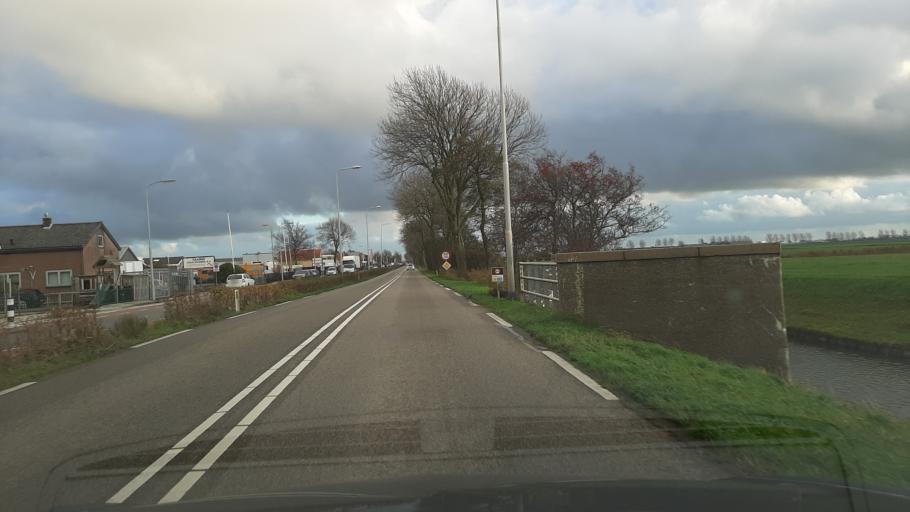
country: NL
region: North Holland
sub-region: Gemeente Haarlemmermeer
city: Hoofddorp
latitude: 52.3647
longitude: 4.7172
